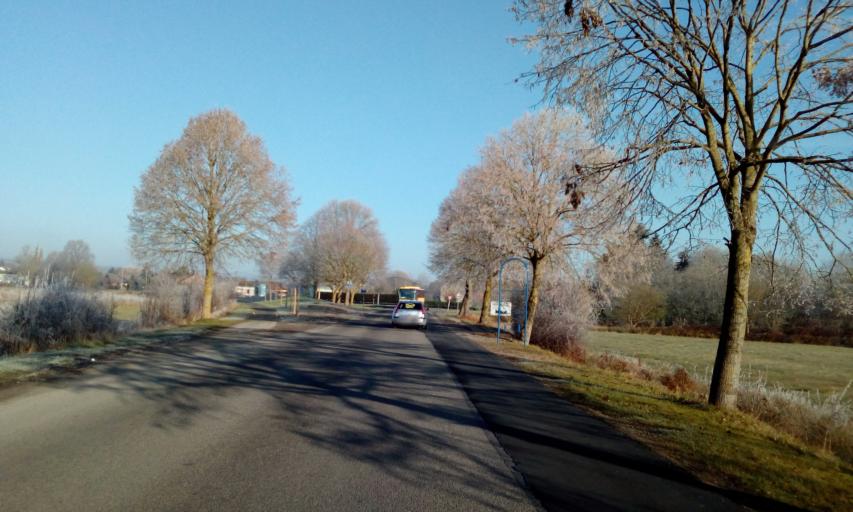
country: BE
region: Wallonia
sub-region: Province de Namur
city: Couvin
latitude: 50.0872
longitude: 4.5207
